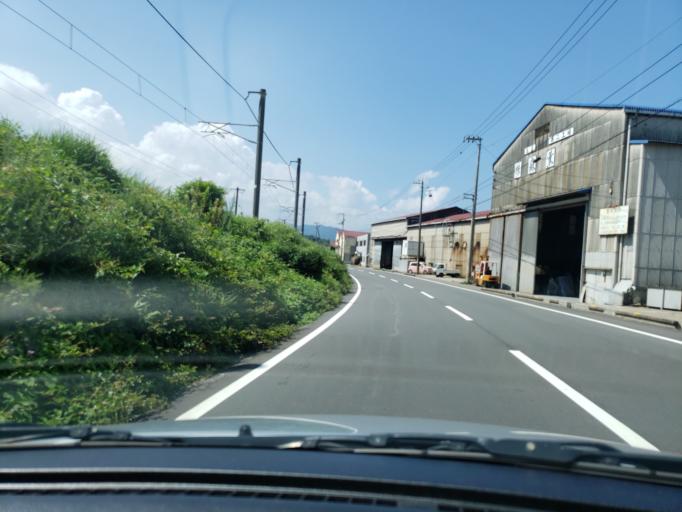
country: JP
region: Ehime
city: Hojo
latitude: 34.0921
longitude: 132.9330
